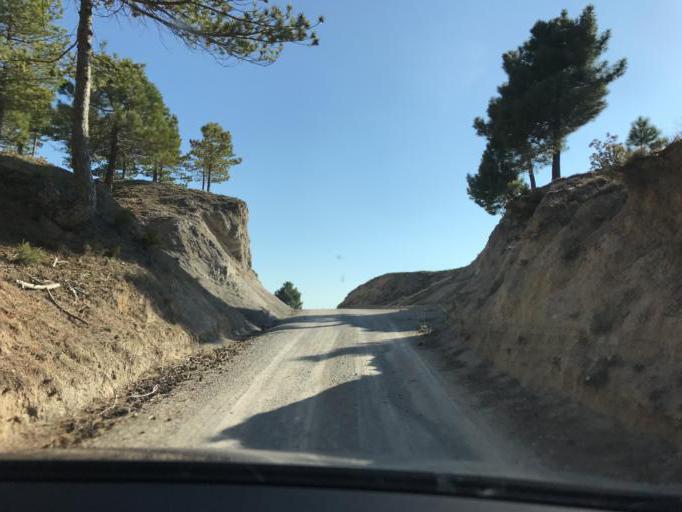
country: ES
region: Andalusia
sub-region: Provincia de Granada
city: Beas de Granada
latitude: 37.2487
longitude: -3.4571
